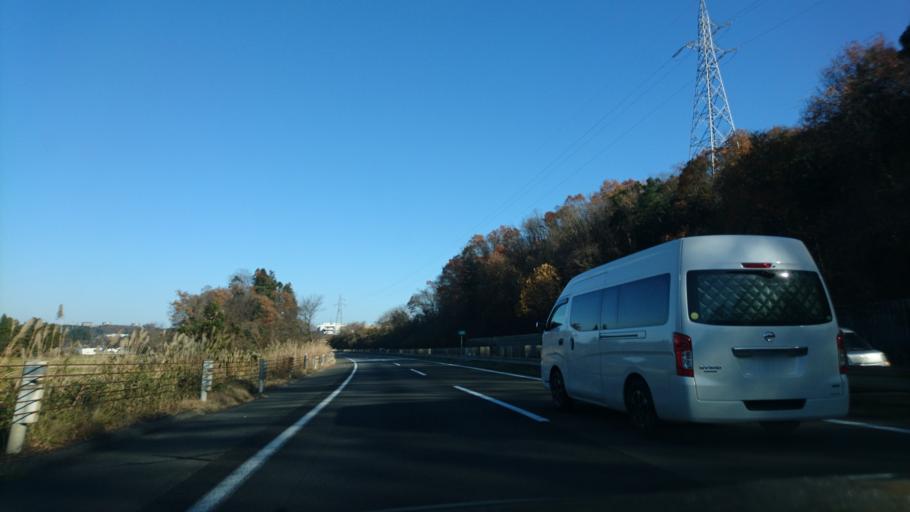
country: JP
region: Miyagi
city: Sendai-shi
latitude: 38.3193
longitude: 140.8380
